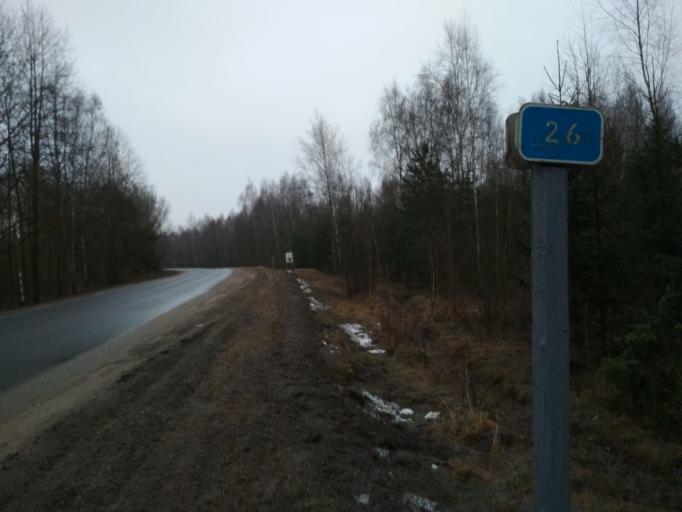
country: BY
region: Minsk
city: Mar''ina Horka
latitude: 53.4915
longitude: 28.1636
